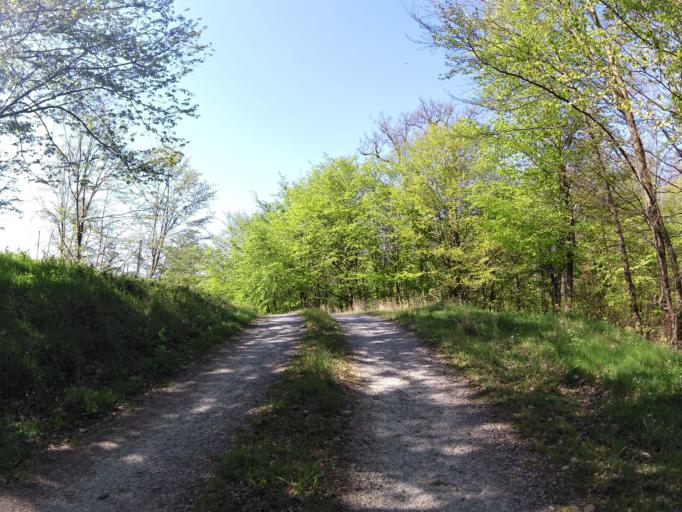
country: DE
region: Thuringia
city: Wolfsburg-Unkeroda
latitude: 50.9739
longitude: 10.2598
